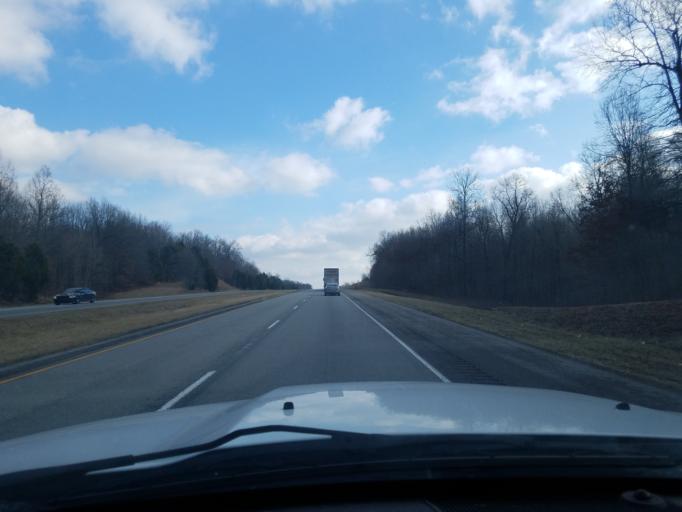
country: US
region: Kentucky
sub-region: Hardin County
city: Elizabethtown
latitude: 37.6378
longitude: -85.8336
